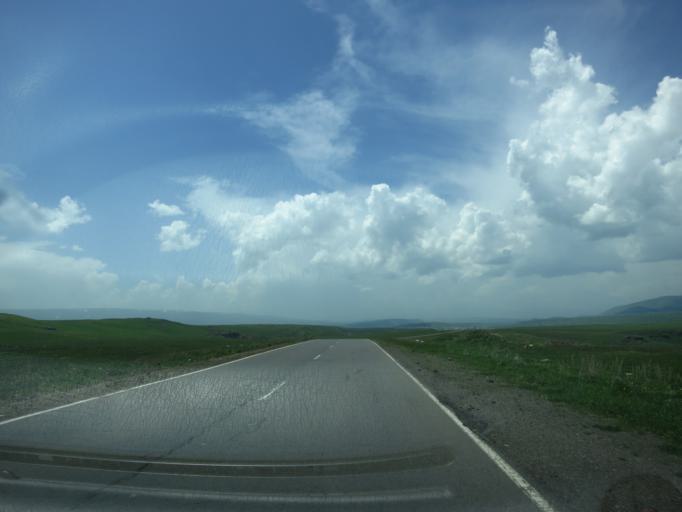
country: GE
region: Samtskhe-Javakheti
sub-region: Ninotsminda
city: Ninotsminda
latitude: 41.2920
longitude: 43.7043
